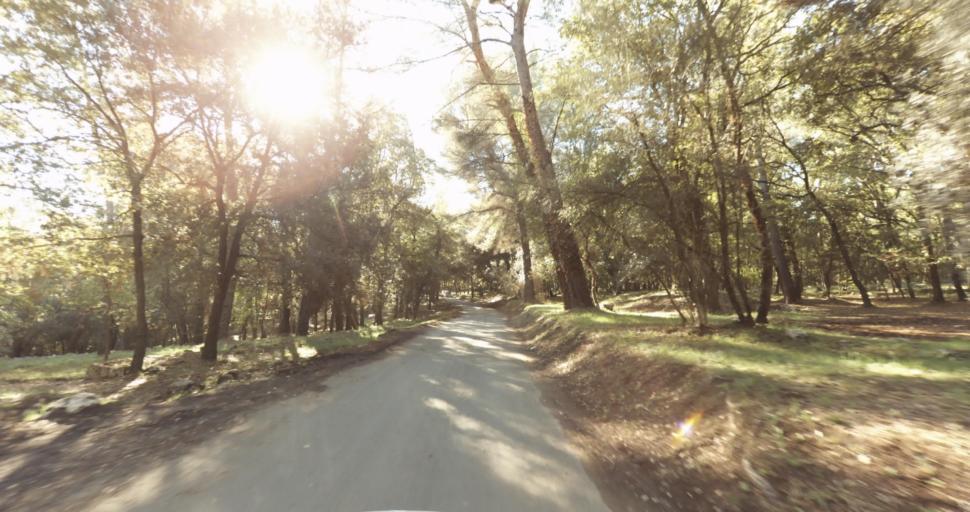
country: FR
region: Provence-Alpes-Cote d'Azur
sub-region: Departement des Alpes-Maritimes
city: Vence
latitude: 43.7099
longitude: 7.0954
